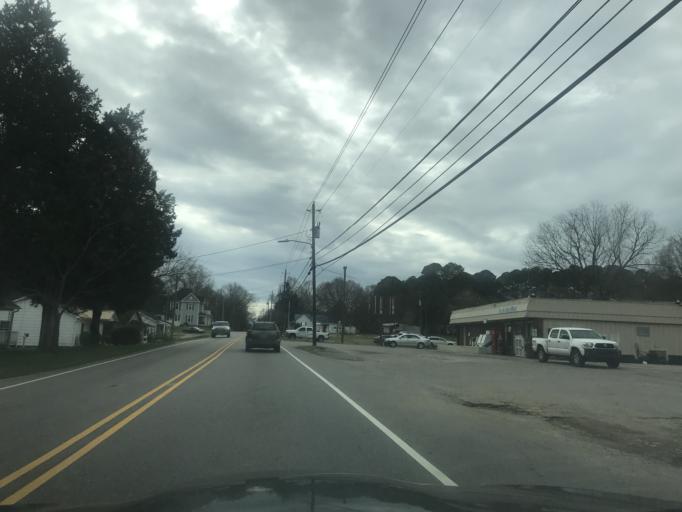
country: US
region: North Carolina
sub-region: Franklin County
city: Franklinton
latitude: 36.1040
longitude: -78.4477
